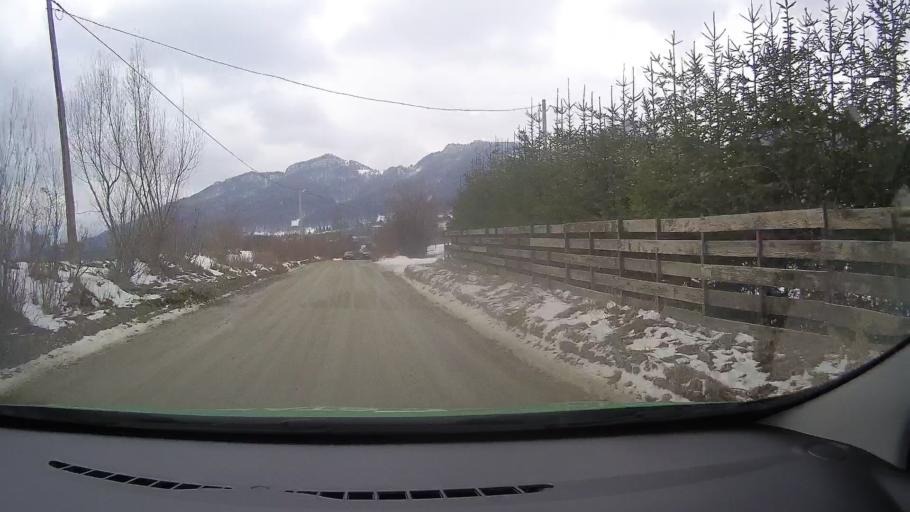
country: RO
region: Brasov
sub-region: Comuna Zarnesti
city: Zarnesti
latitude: 45.5463
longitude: 25.3224
